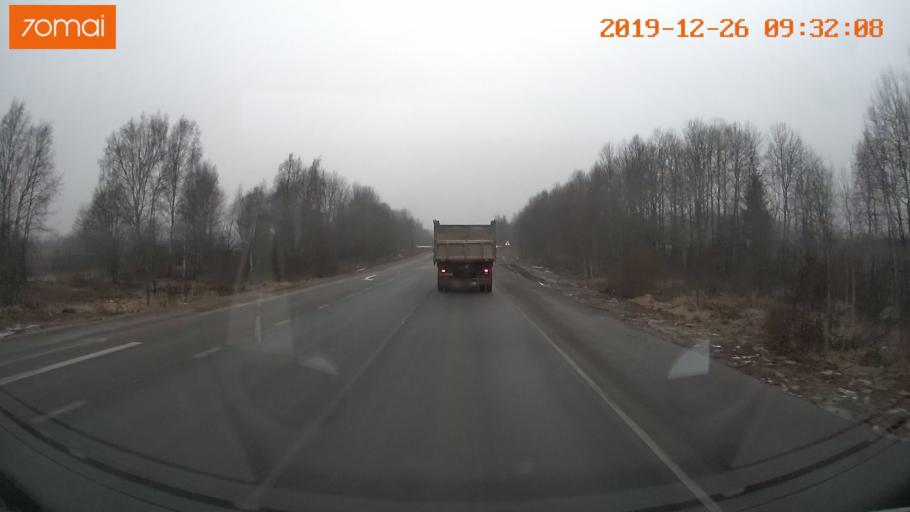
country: RU
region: Vologda
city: Gryazovets
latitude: 59.0750
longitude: 40.1202
